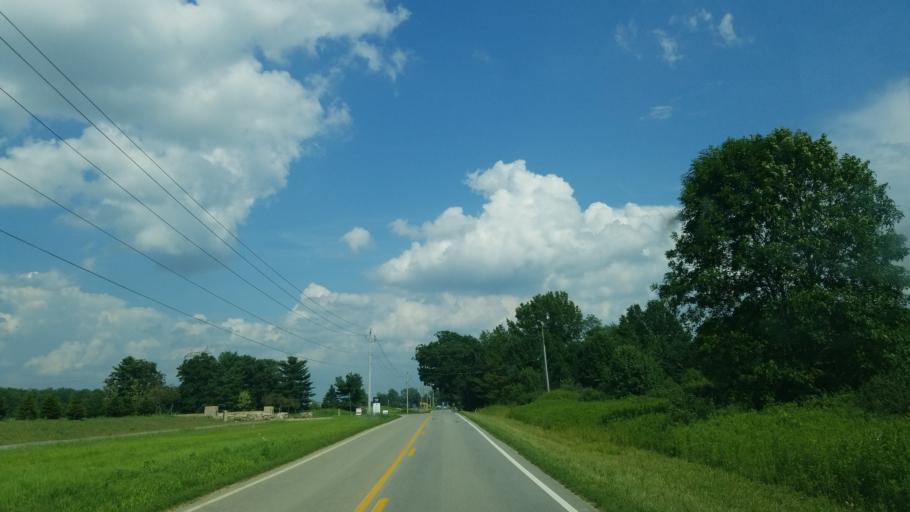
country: US
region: Ohio
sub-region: Delaware County
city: Powell
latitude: 40.2172
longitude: -83.1154
